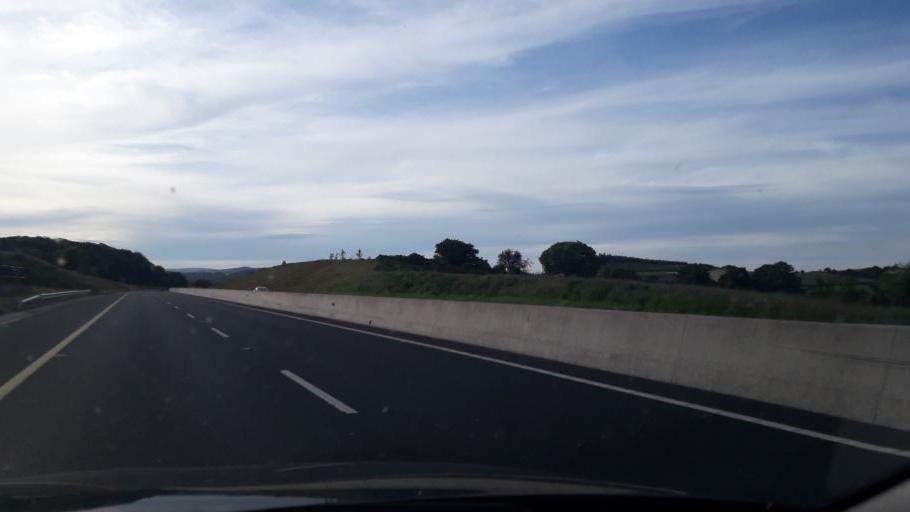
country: IE
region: Leinster
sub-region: Wicklow
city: Rathnew
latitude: 52.9191
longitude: -6.1136
